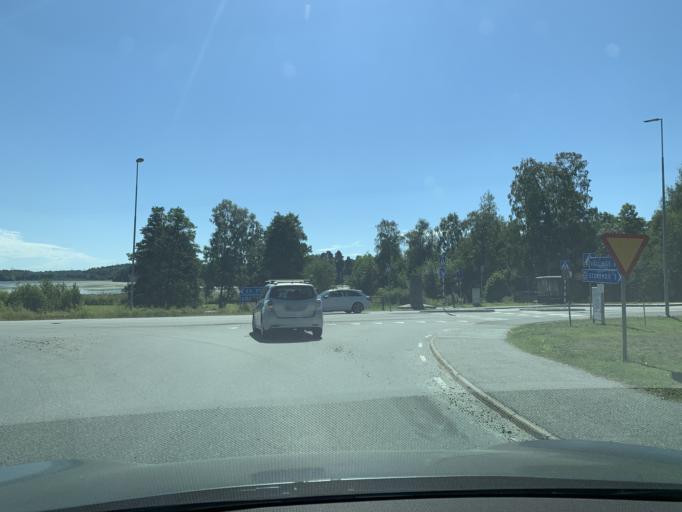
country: SE
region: Stockholm
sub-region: Botkyrka Kommun
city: Eriksberg
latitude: 59.2422
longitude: 17.7859
